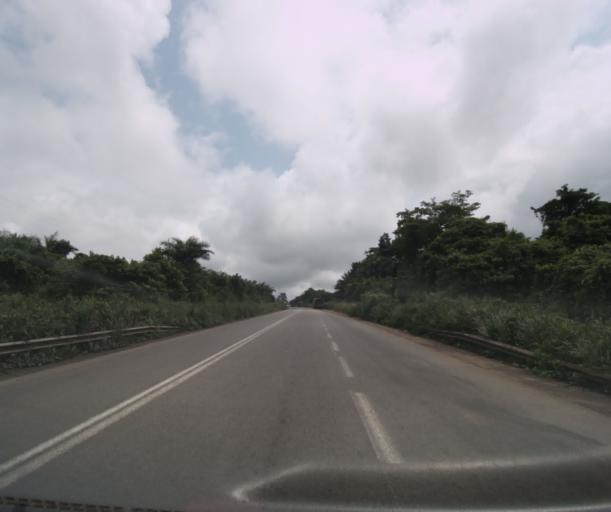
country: CM
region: Littoral
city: Edea
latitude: 3.7808
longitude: 10.1576
